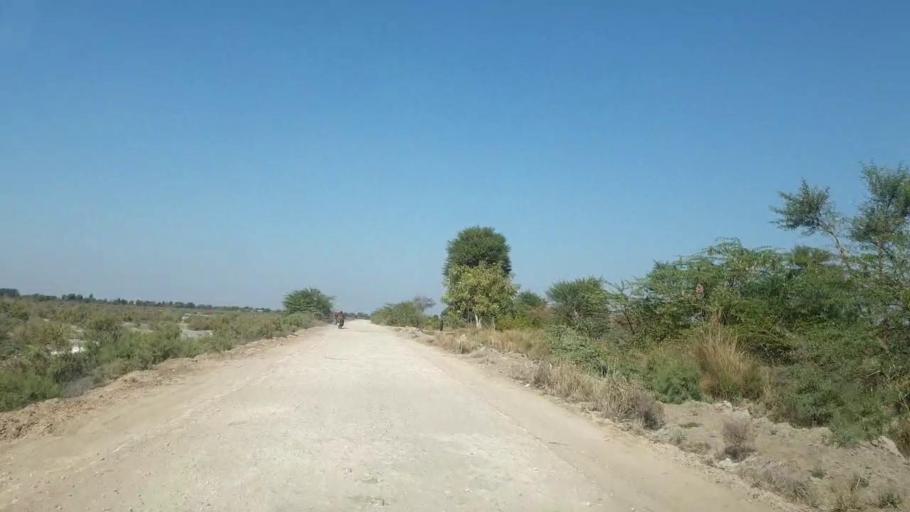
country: PK
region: Sindh
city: Mirpur Khas
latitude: 25.6649
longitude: 69.0267
